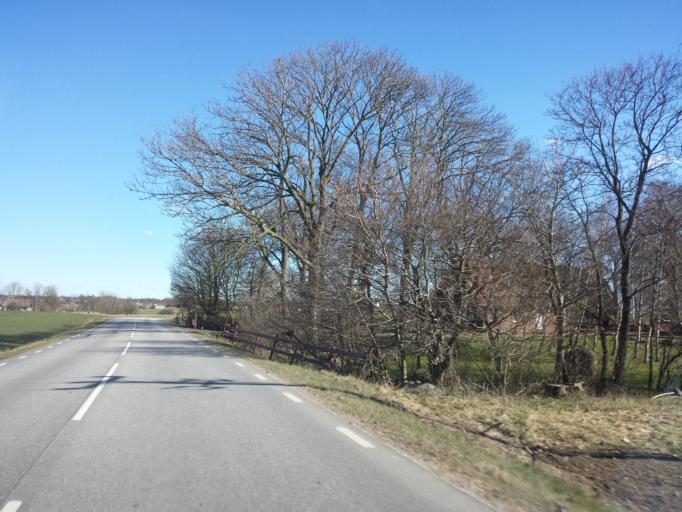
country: SE
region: Skane
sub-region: Tomelilla Kommun
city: Tomelilla
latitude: 55.6386
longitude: 13.8801
